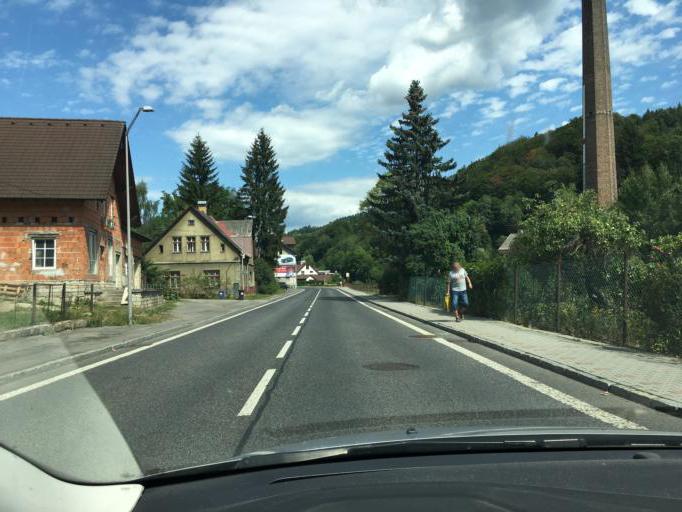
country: CZ
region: Liberecky
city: Velke Hamry
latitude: 50.7212
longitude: 15.3155
